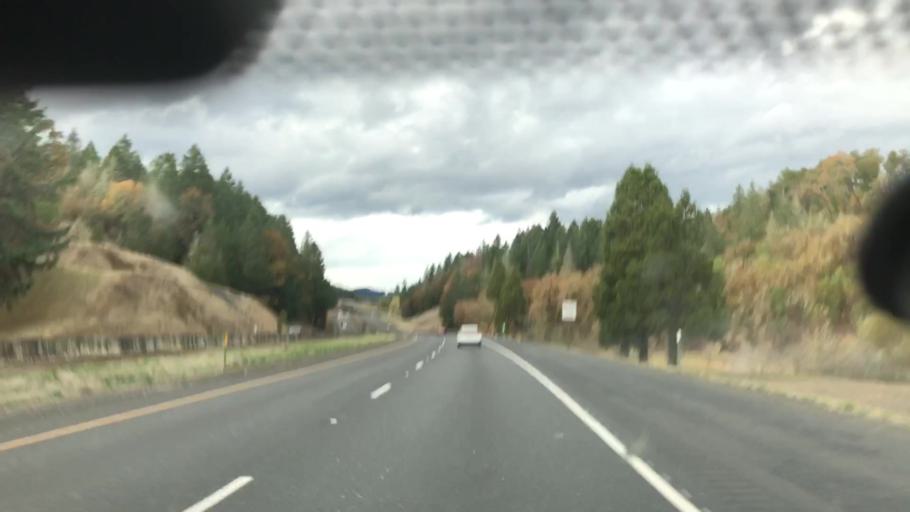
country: US
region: Oregon
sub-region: Douglas County
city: Sutherlin
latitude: 43.4837
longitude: -123.3247
